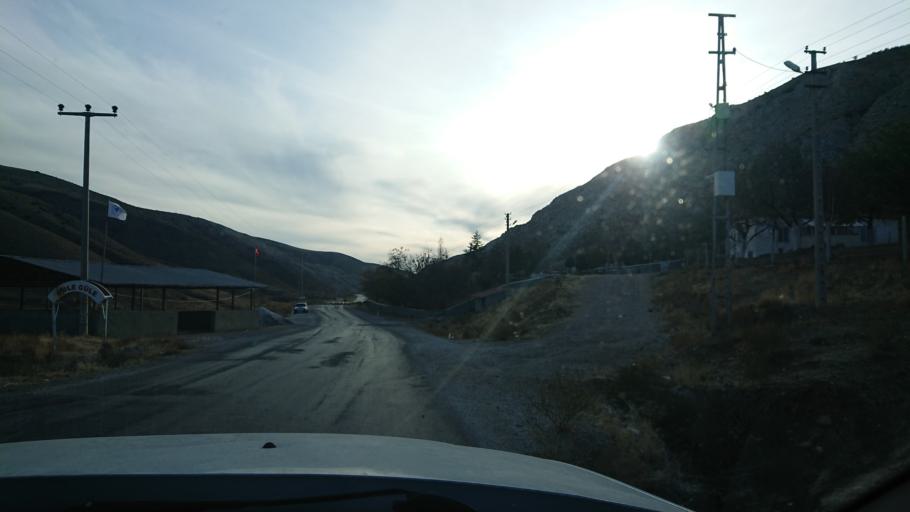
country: TR
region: Ankara
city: Sereflikochisar
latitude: 38.7614
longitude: 33.6974
